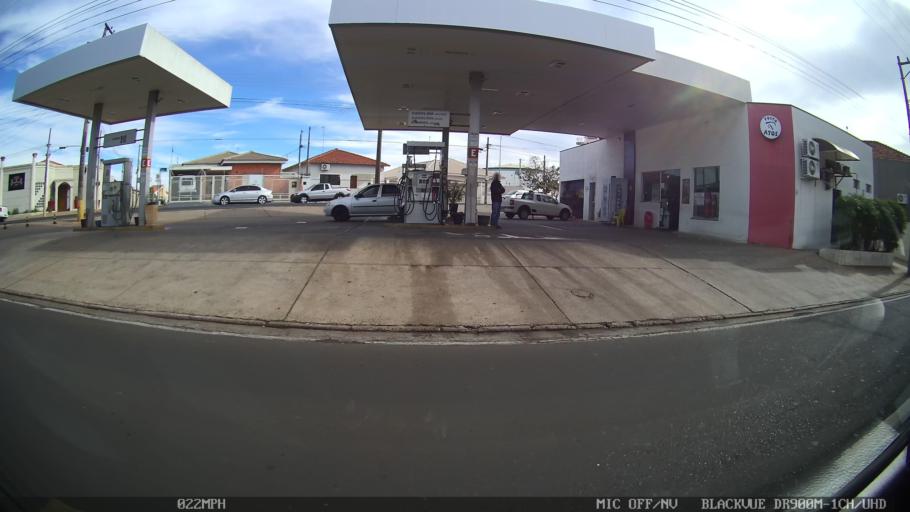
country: BR
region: Sao Paulo
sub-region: Catanduva
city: Catanduva
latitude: -21.1424
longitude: -48.9827
